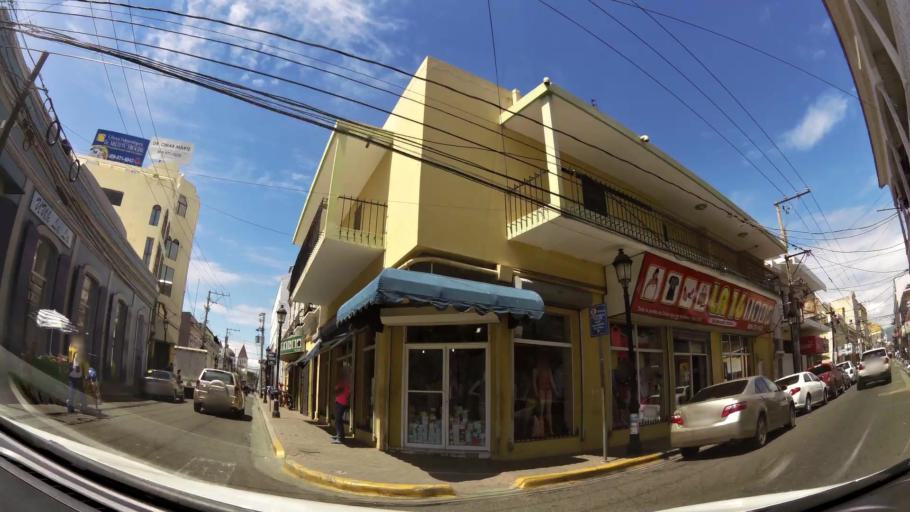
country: DO
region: Santiago
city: Santiago de los Caballeros
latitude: 19.4498
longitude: -70.7039
